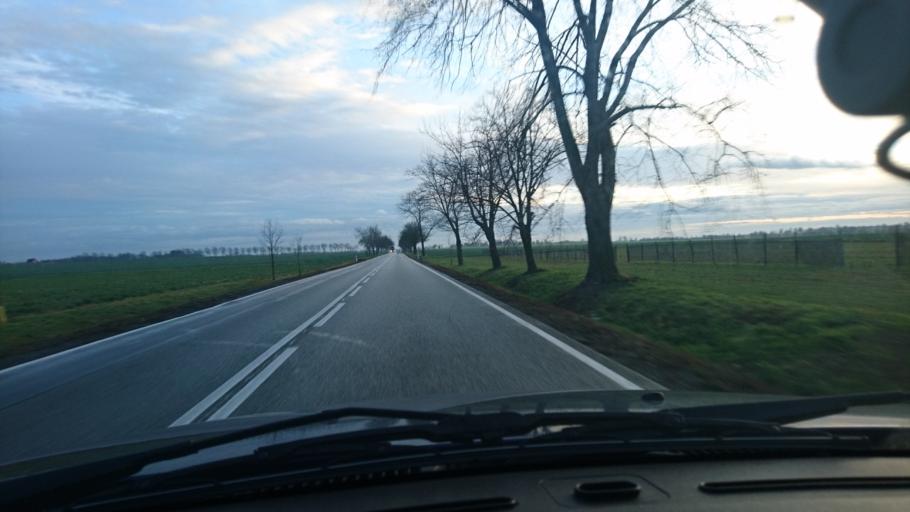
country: PL
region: Opole Voivodeship
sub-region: Powiat kluczborski
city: Byczyna
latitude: 51.0793
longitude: 18.2000
